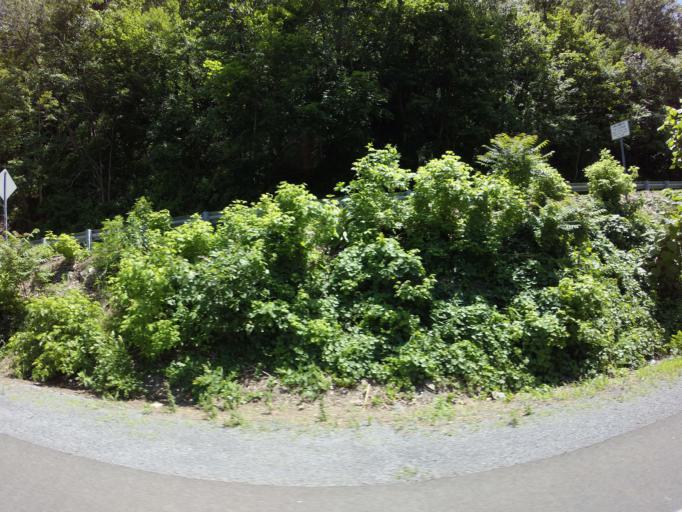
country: US
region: West Virginia
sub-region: Jefferson County
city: Bolivar
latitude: 39.3199
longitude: -77.7313
